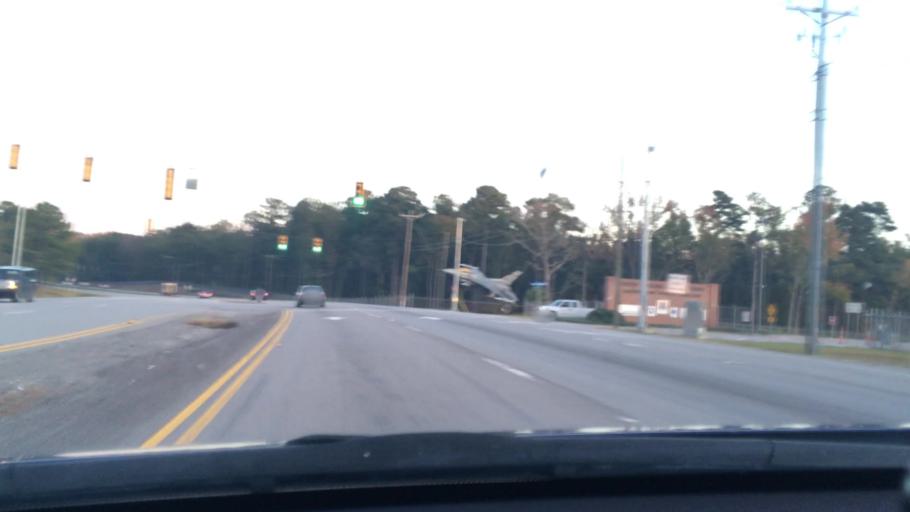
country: US
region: South Carolina
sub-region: Richland County
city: Hopkins
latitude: 33.9407
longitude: -80.8015
